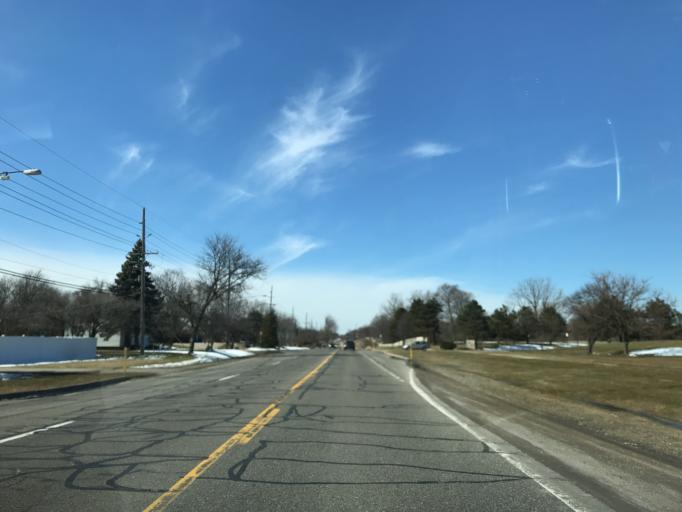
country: US
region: Michigan
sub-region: Oakland County
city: Franklin
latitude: 42.4854
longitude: -83.3301
